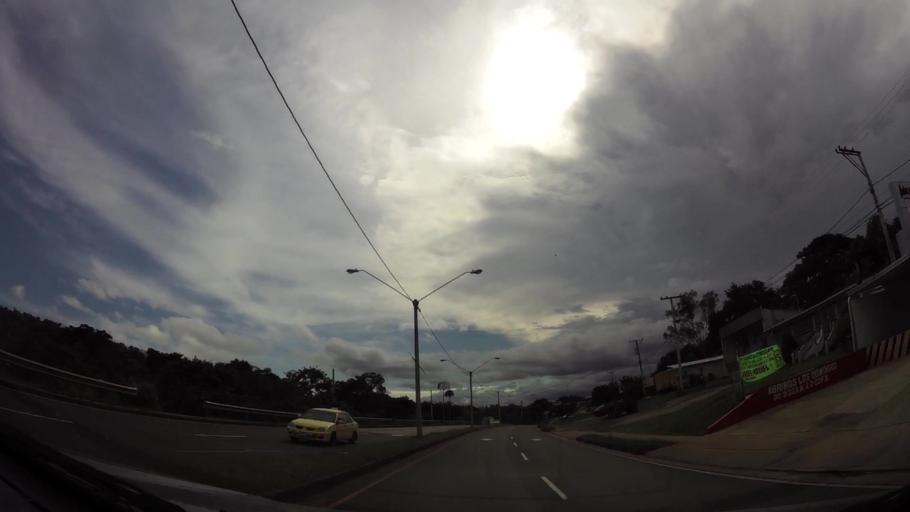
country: PA
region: Panama
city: El Coco
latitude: 8.8647
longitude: -79.8037
